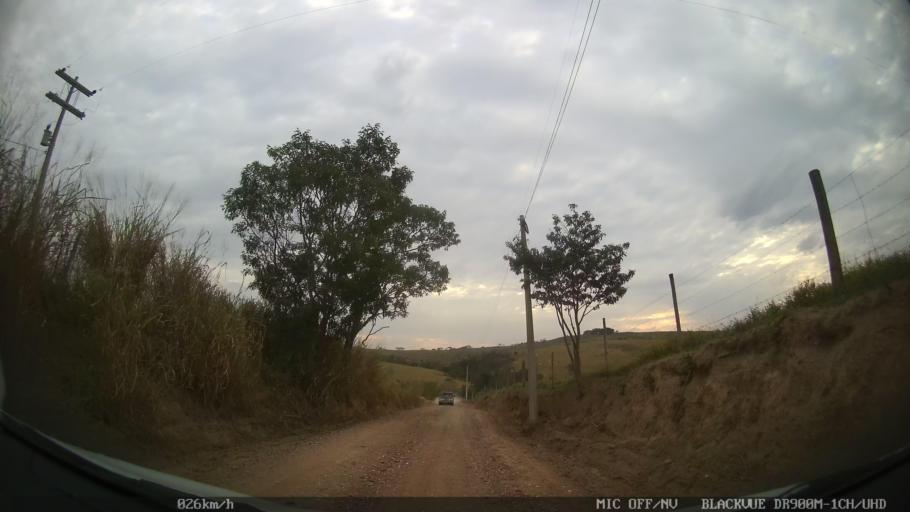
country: BR
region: Sao Paulo
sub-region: Americana
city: Americana
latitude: -22.6792
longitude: -47.3768
